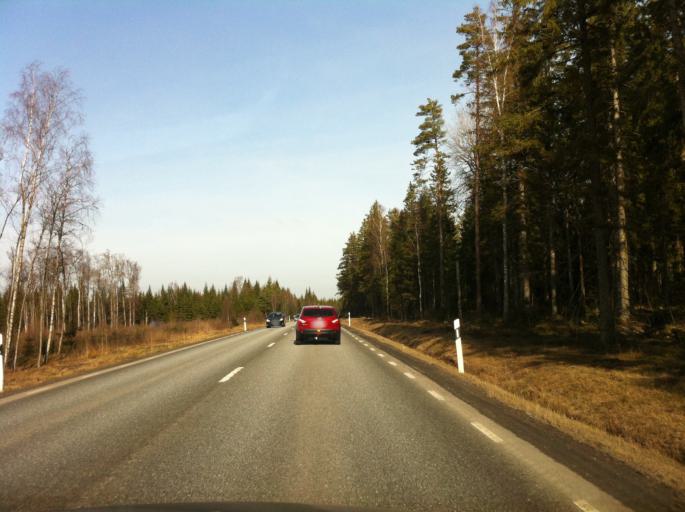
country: SE
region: Joenkoeping
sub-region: Mullsjo Kommun
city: Mullsjoe
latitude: 58.0227
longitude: 13.8295
